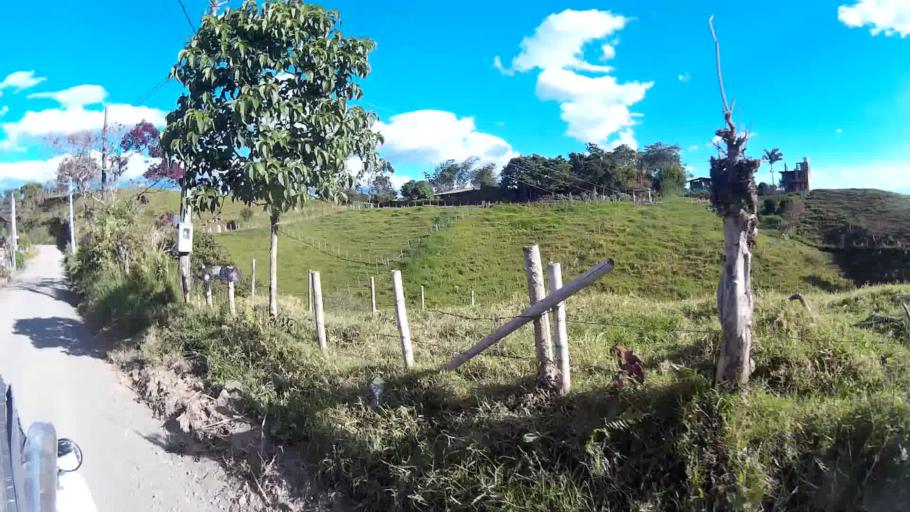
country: CO
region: Quindio
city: Filandia
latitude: 4.7172
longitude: -75.6793
